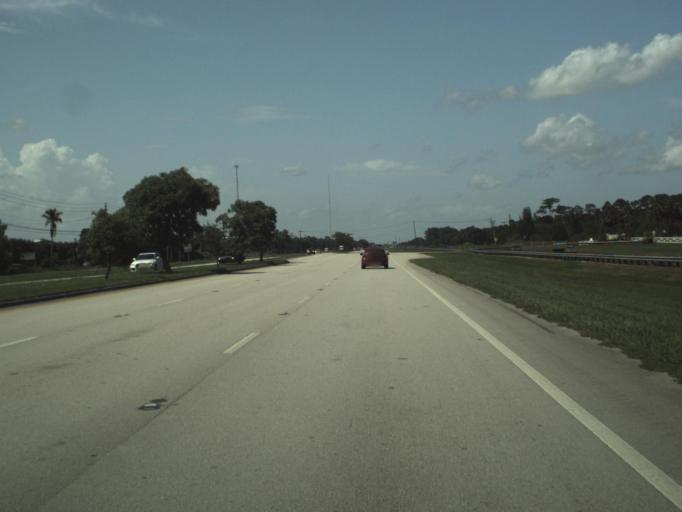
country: US
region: Florida
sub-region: Palm Beach County
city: Villages of Oriole
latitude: 26.5517
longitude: -80.2056
